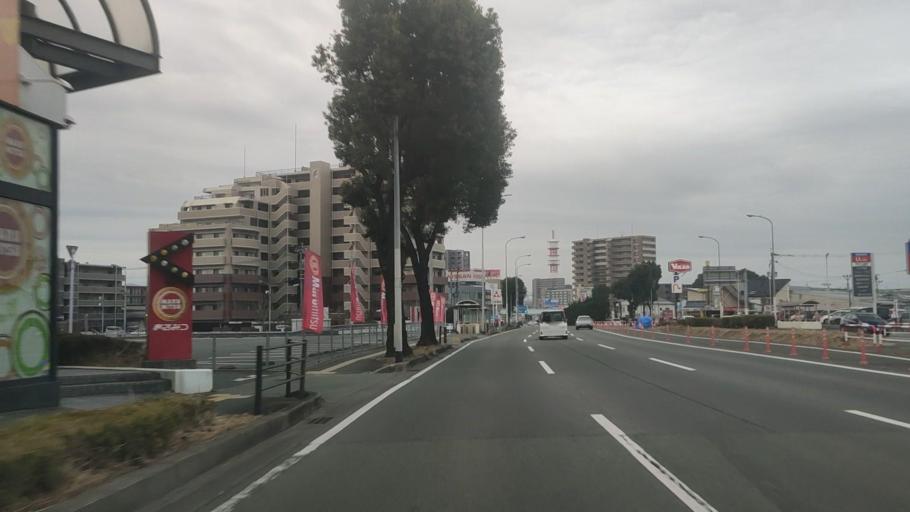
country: JP
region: Kumamoto
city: Kumamoto
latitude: 32.8148
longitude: 130.7497
